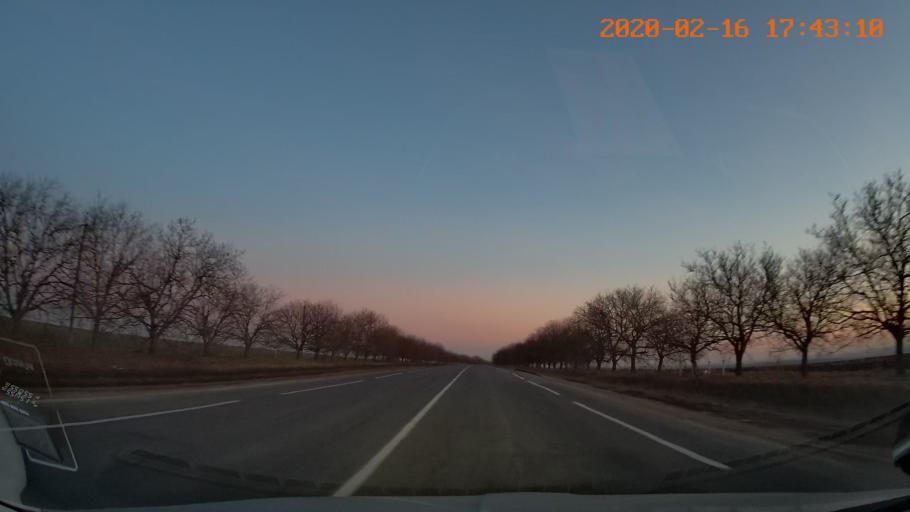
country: MD
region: Riscani
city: Riscani
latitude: 48.0168
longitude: 27.5626
